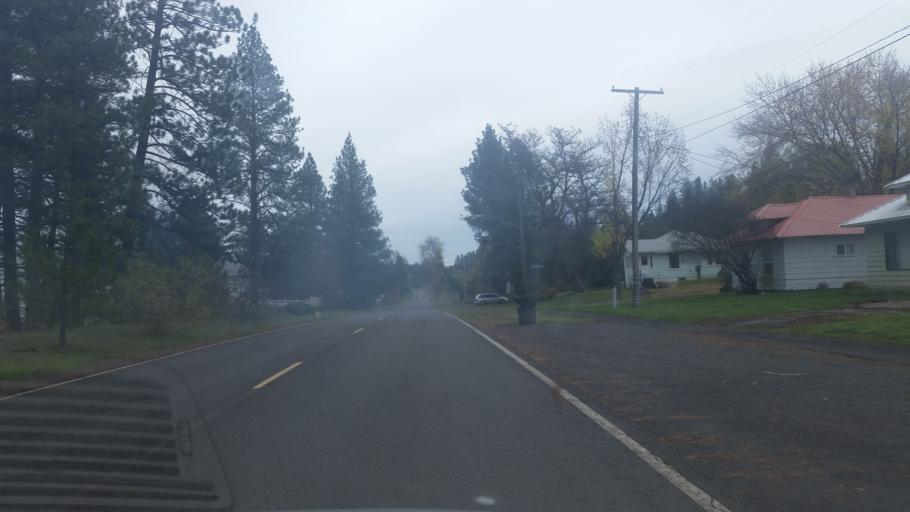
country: US
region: Washington
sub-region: Spokane County
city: Cheney
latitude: 47.2297
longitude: -117.4693
